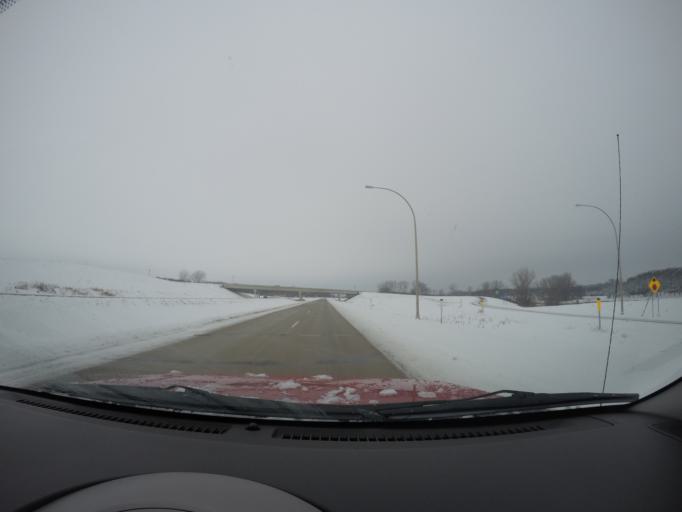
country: US
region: Minnesota
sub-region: Olmsted County
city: Rochester
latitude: 43.9578
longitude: -92.3764
